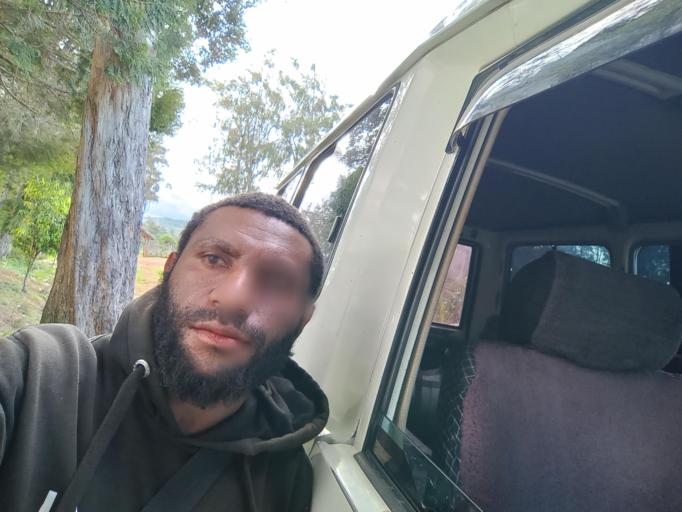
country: PG
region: Southern Highlands
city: Ialibu
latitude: -6.1599
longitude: 144.0217
